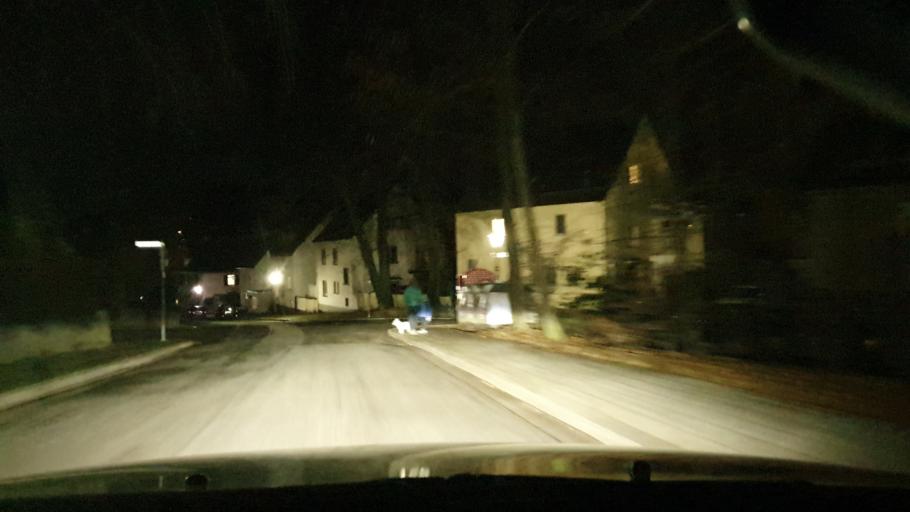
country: DE
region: Rheinland-Pfalz
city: Kaiserslautern
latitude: 49.4315
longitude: 7.7692
